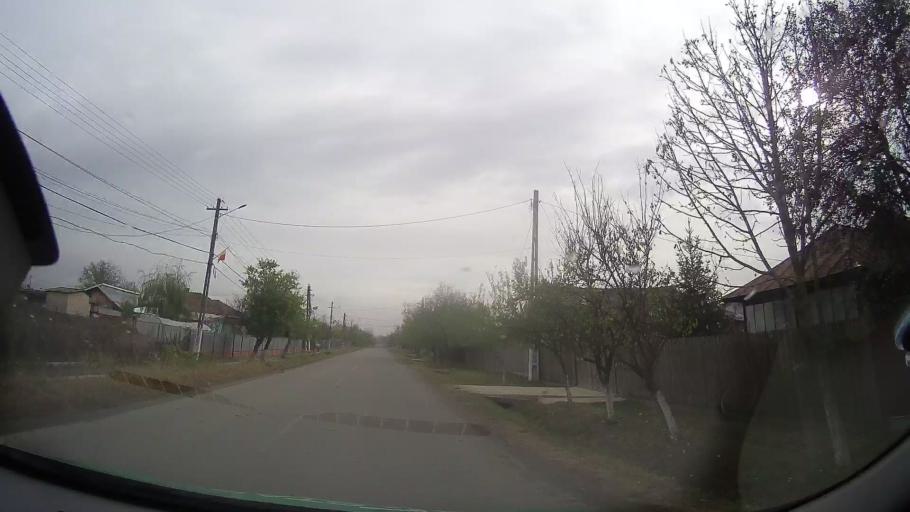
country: RO
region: Prahova
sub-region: Comuna Dumbrava
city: Dumbrava
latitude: 44.8687
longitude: 26.1967
